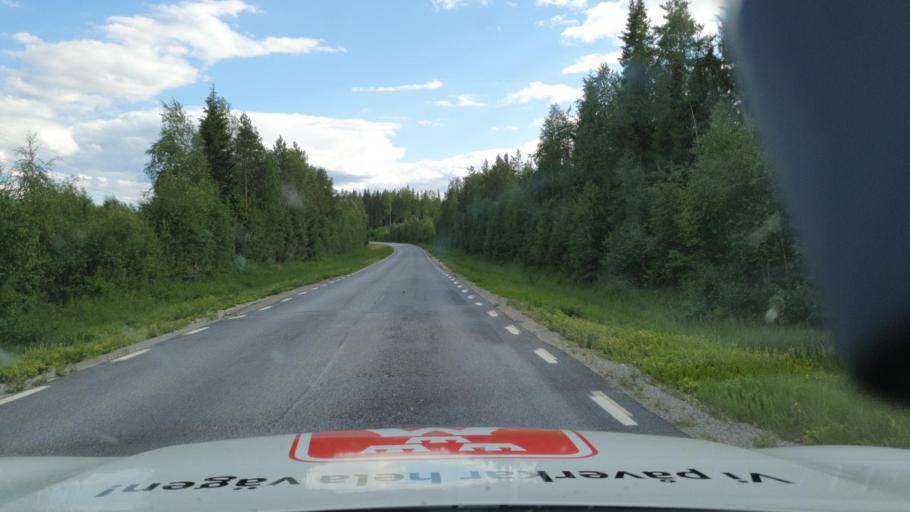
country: SE
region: Vaesterbotten
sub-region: Skelleftea Kommun
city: Langsele
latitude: 64.5779
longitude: 19.9263
